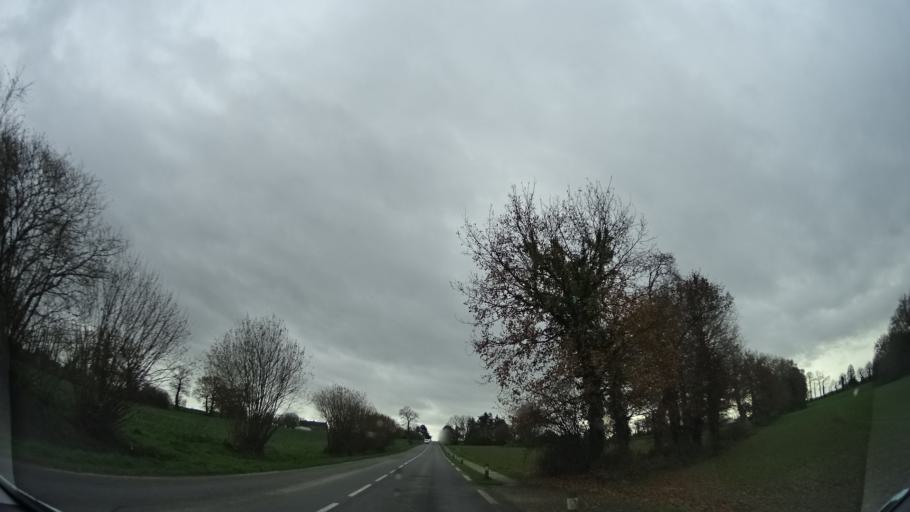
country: FR
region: Brittany
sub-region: Departement des Cotes-d'Armor
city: Lanvallay
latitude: 48.4432
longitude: -2.0193
